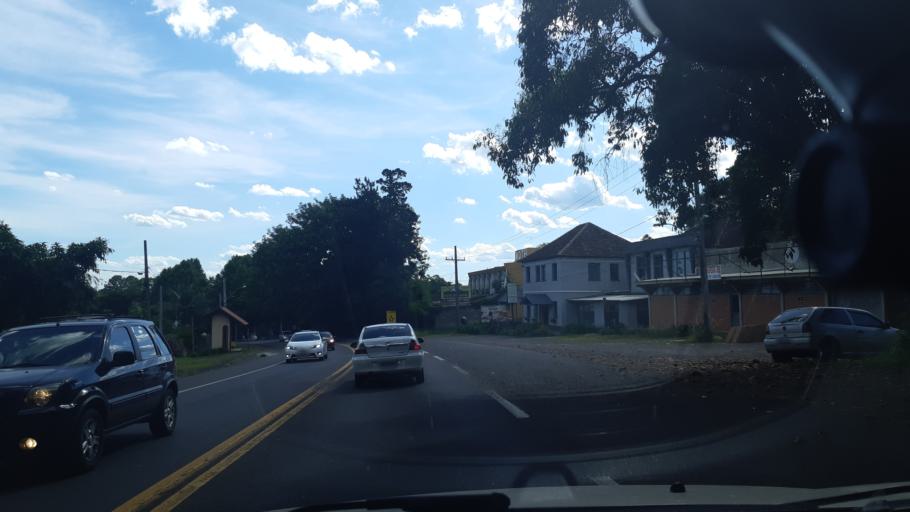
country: BR
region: Rio Grande do Sul
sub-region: Ivoti
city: Ivoti
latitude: -29.6220
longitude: -51.1298
